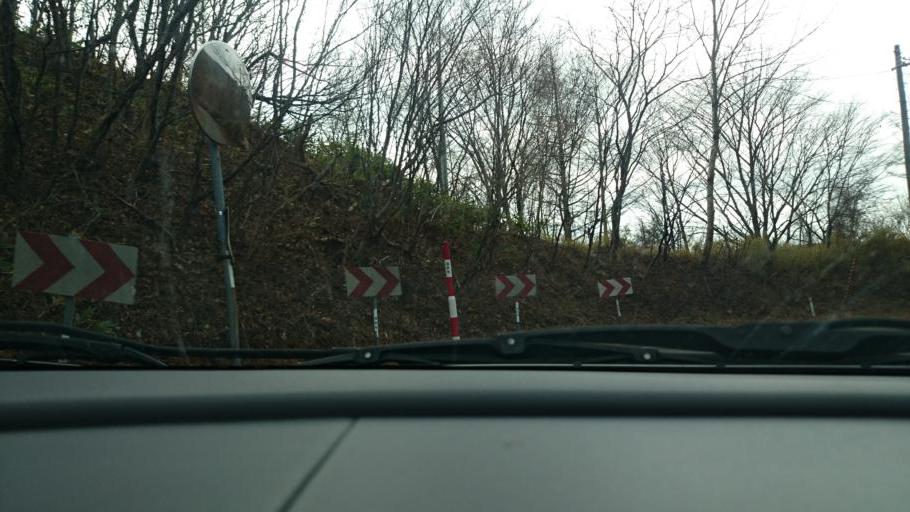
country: JP
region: Tochigi
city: Kuroiso
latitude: 37.1590
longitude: 140.0218
